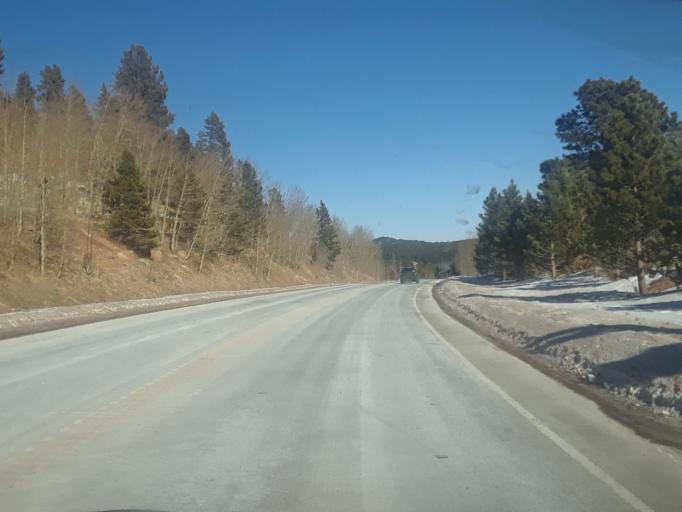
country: US
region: Colorado
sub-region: Boulder County
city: Nederland
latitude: 40.0932
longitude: -105.4933
